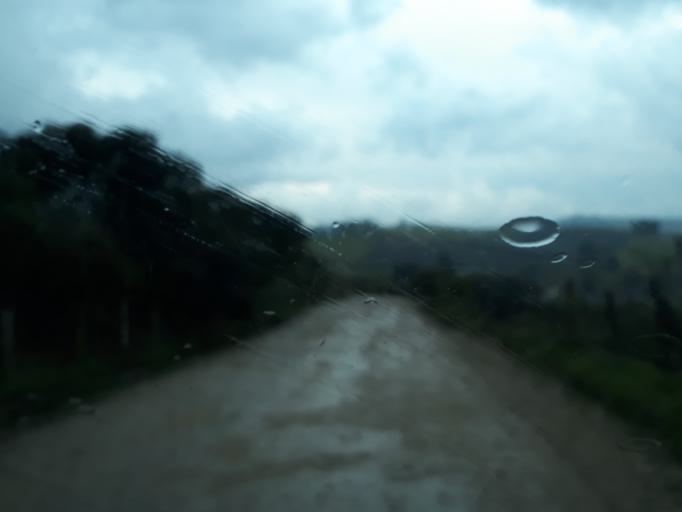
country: CO
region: Cundinamarca
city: Villapinzon
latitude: 5.3044
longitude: -73.5897
